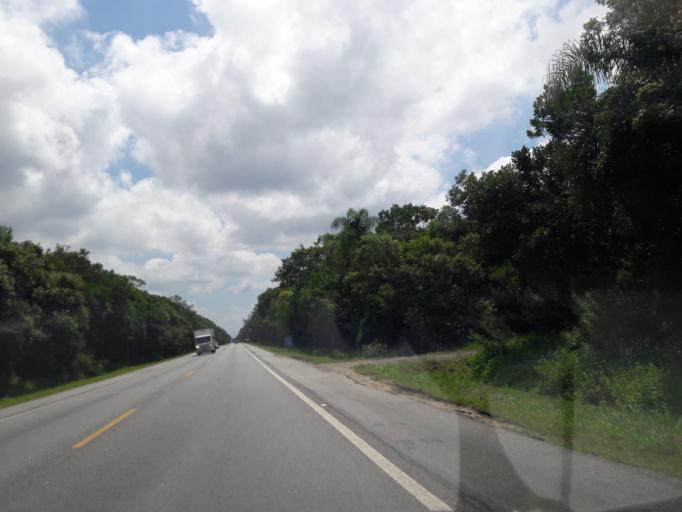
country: BR
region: Parana
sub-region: Pontal Do Parana
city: Pontal do Parana
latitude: -25.6322
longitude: -48.5384
